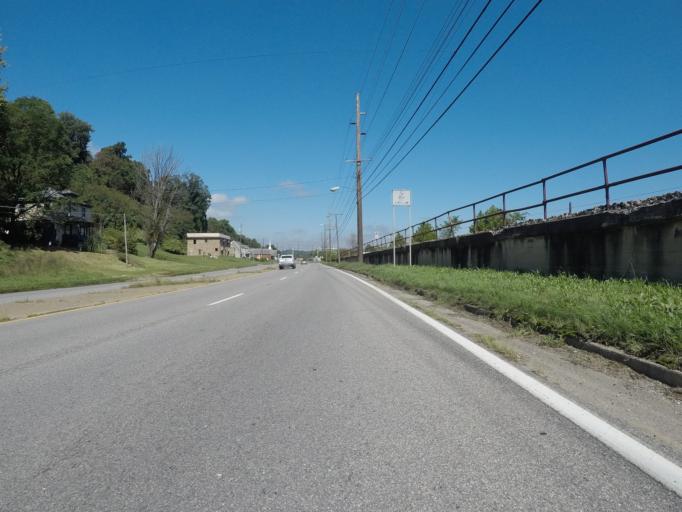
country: US
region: Ohio
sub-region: Lawrence County
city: South Point
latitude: 38.4300
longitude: -82.6034
